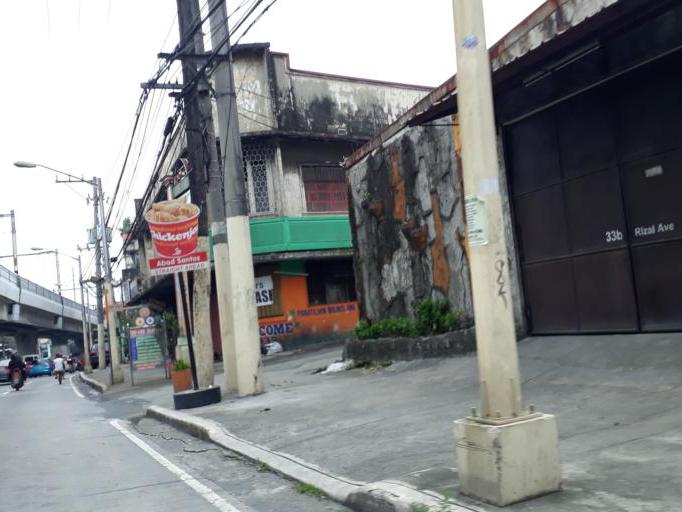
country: PH
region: Metro Manila
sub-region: City of Manila
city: Manila
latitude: 14.6383
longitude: 120.9832
